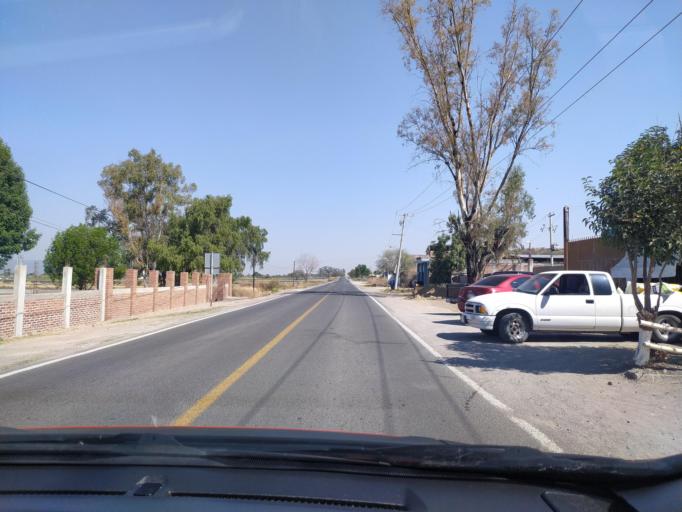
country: MX
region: Guanajuato
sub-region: San Francisco del Rincon
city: San Ignacio de Hidalgo
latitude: 20.8596
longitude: -101.8608
